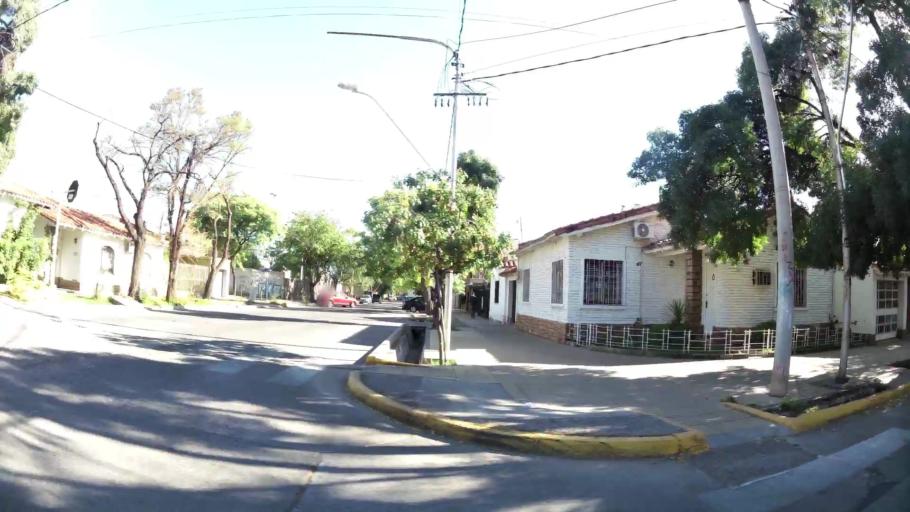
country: AR
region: Mendoza
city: Las Heras
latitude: -32.8665
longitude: -68.8527
